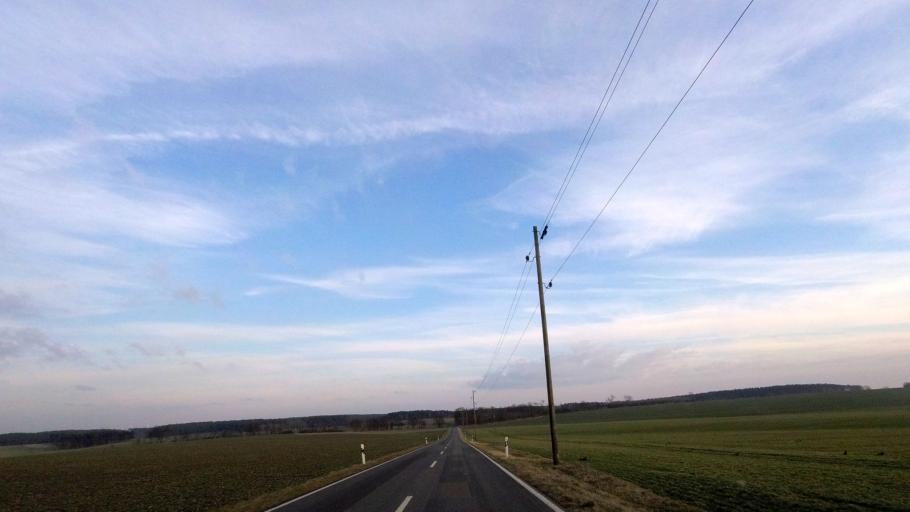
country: DE
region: Brandenburg
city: Belzig
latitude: 52.0958
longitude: 12.5714
